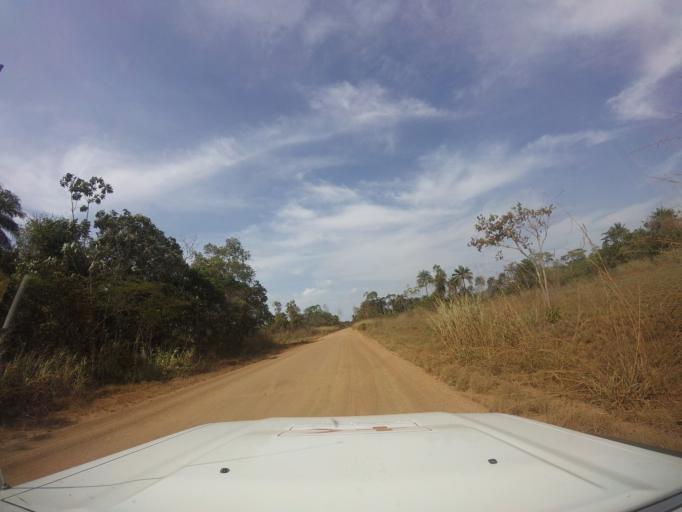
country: LR
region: Grand Cape Mount
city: Robertsport
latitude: 6.6760
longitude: -11.1390
